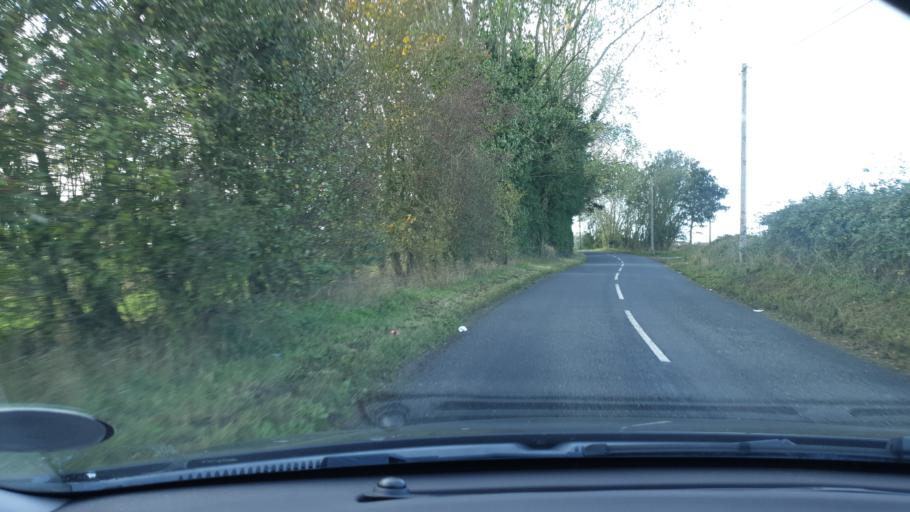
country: GB
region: England
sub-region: Essex
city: Manningtree
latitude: 51.9294
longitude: 1.0490
